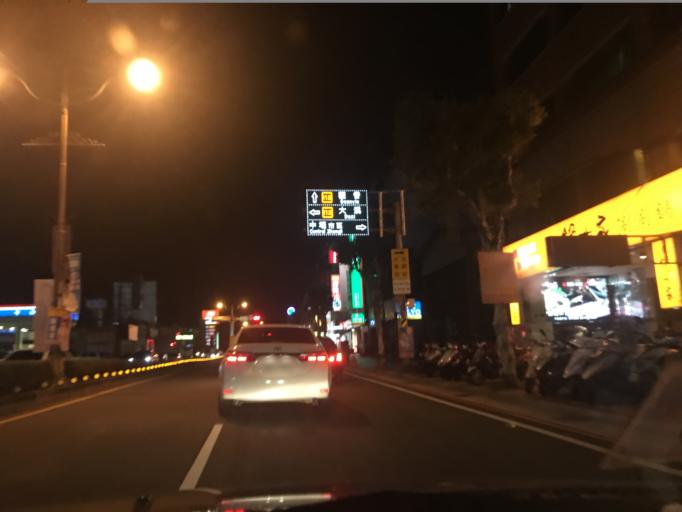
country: TW
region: Taiwan
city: Taoyuan City
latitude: 24.9452
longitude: 121.2305
